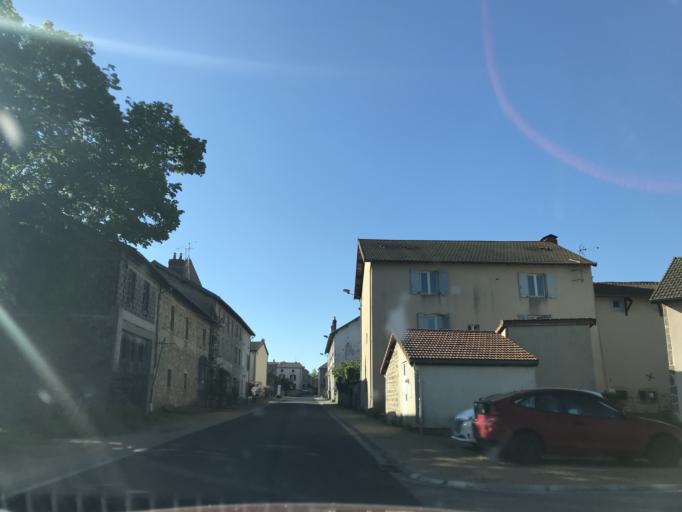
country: FR
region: Auvergne
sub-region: Departement du Puy-de-Dome
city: Job
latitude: 45.6193
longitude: 3.6796
